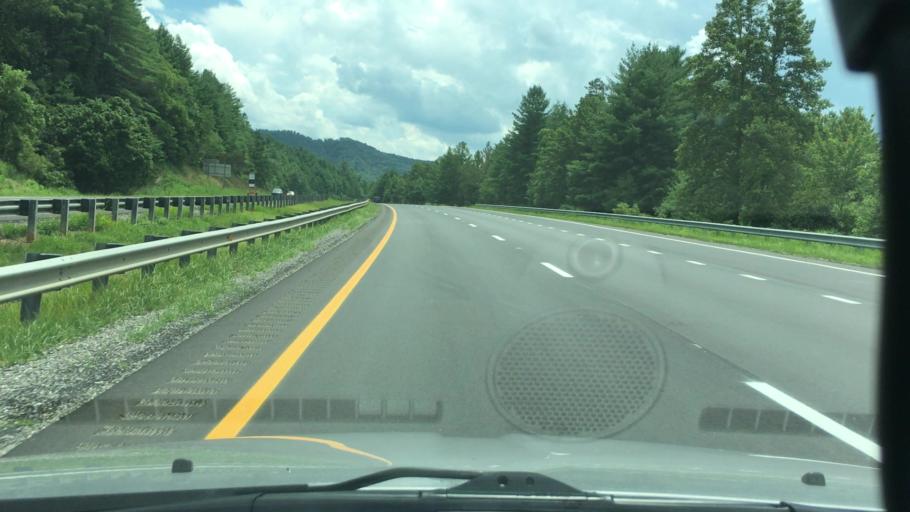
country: US
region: North Carolina
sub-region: Madison County
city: Mars Hill
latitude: 35.7803
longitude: -82.5400
